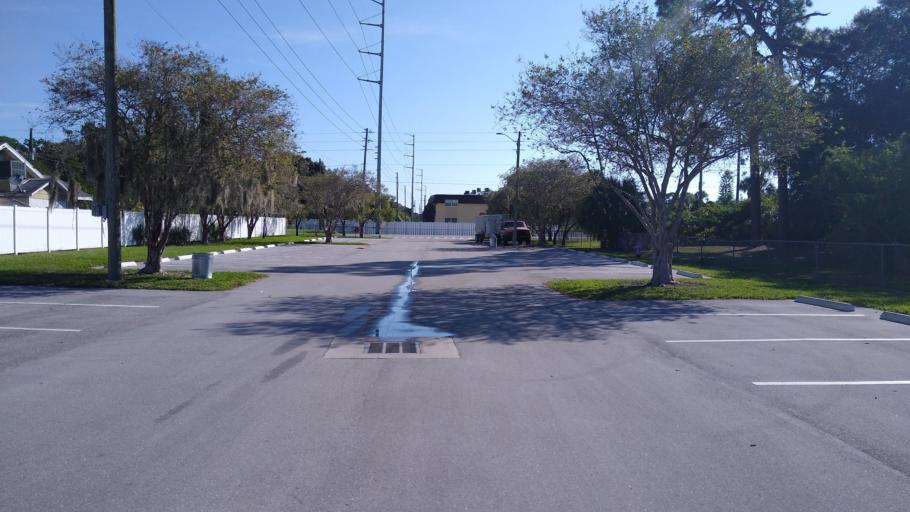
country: US
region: Florida
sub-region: Pinellas County
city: Largo
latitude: 27.9237
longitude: -82.7689
